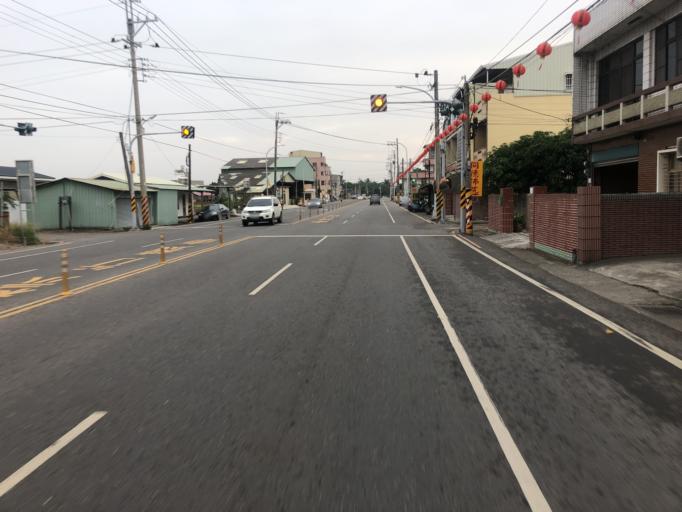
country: TW
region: Taiwan
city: Xinying
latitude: 23.1499
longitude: 120.2876
